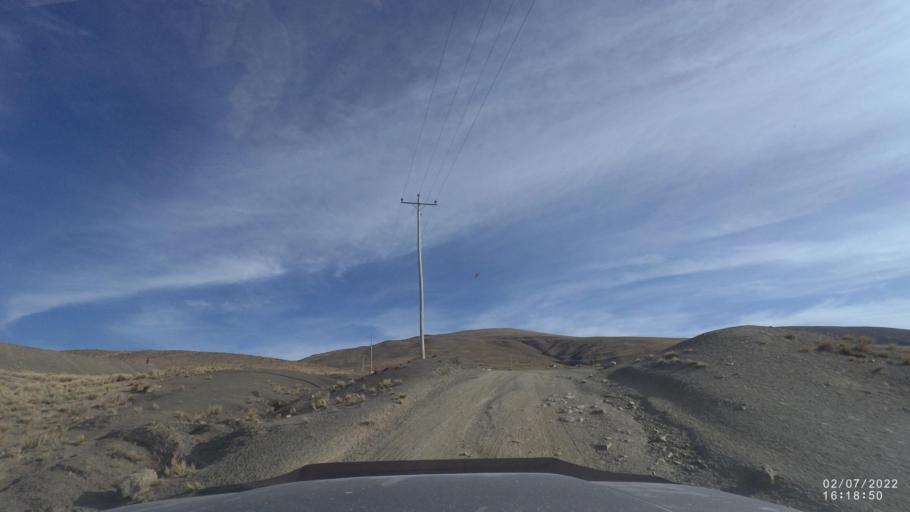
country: BO
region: Cochabamba
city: Irpa Irpa
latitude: -17.9280
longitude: -66.4428
